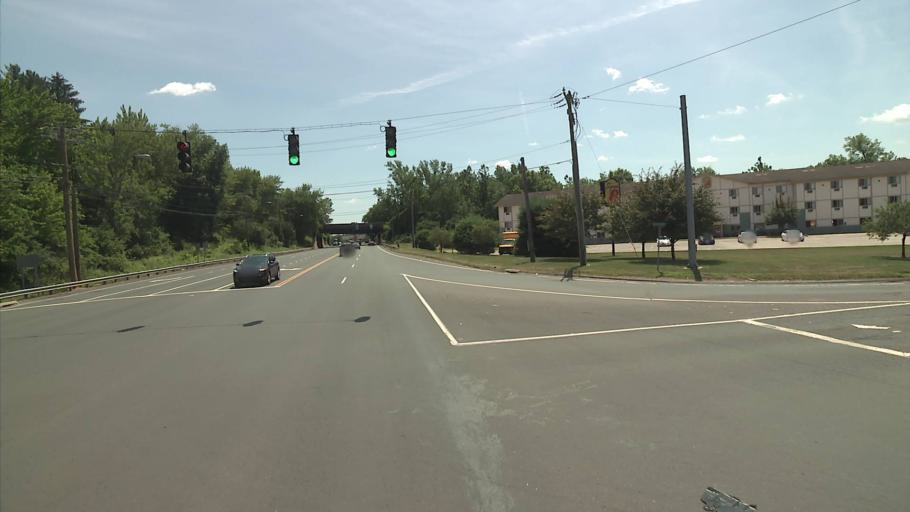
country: US
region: Connecticut
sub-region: Middlesex County
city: Cromwell
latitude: 41.6048
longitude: -72.7063
